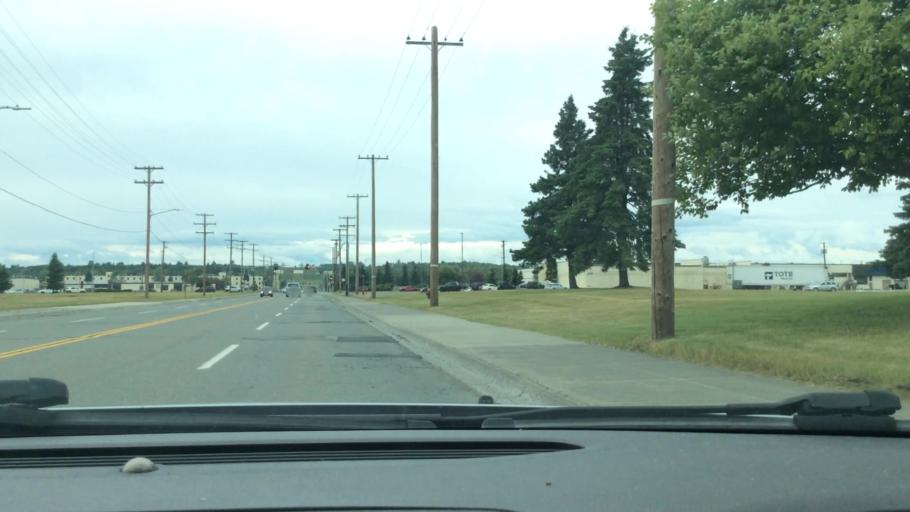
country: US
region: Alaska
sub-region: Anchorage Municipality
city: Anchorage
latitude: 61.2352
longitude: -149.8493
